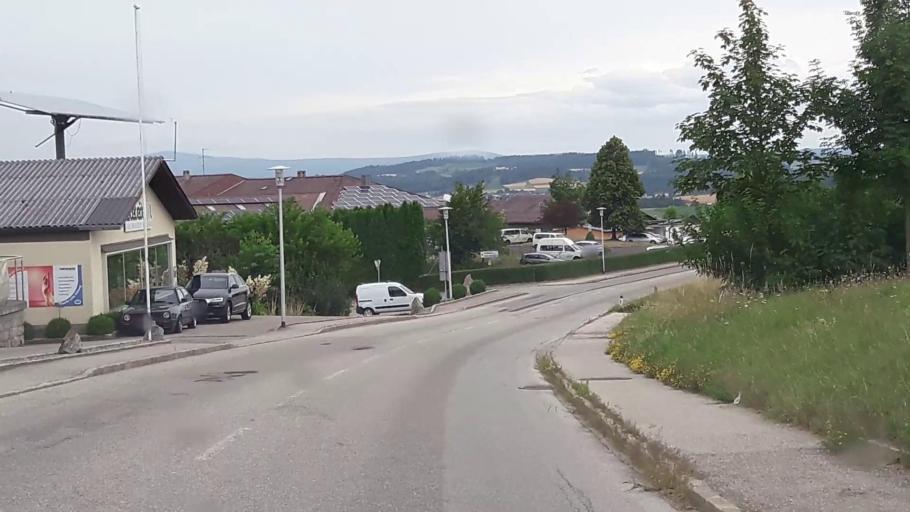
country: AT
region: Upper Austria
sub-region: Politischer Bezirk Rohrbach
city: Kleinzell im Muehlkreis
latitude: 48.4875
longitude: 13.9680
